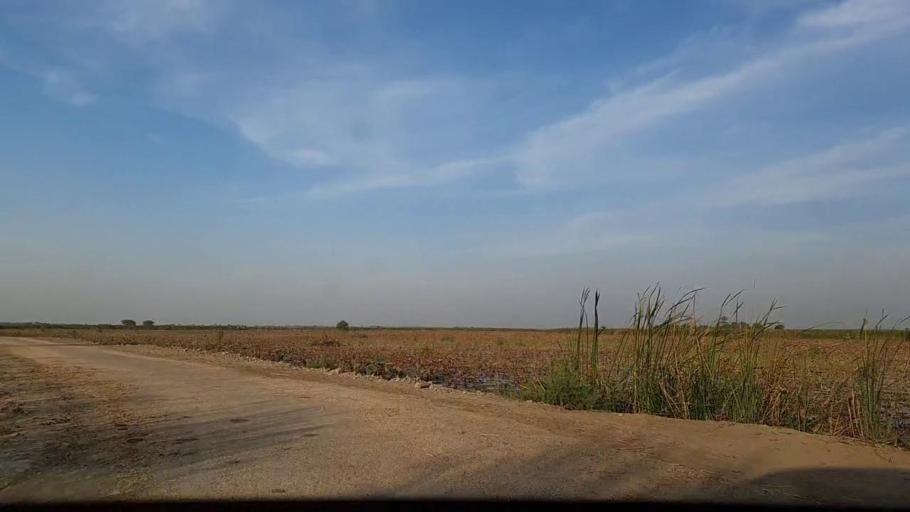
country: PK
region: Sindh
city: Mirpur Batoro
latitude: 24.6546
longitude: 68.1464
